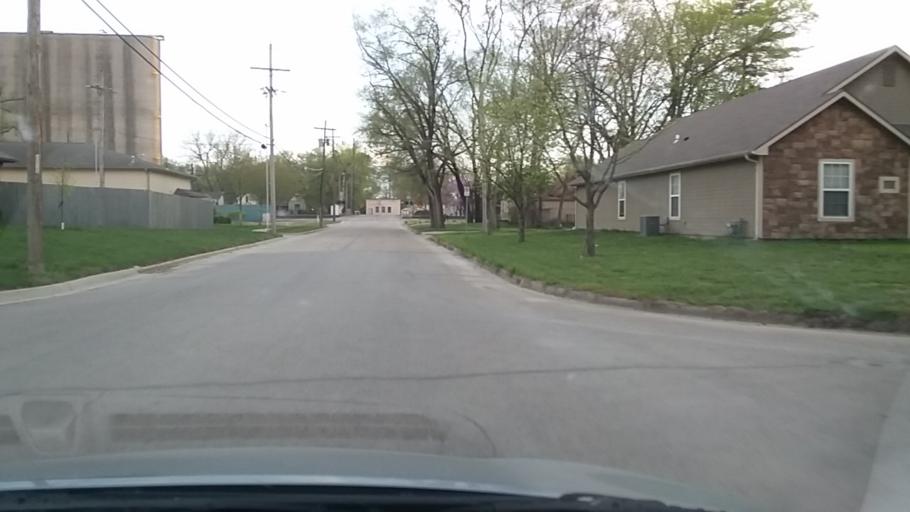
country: US
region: Kansas
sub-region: Douglas County
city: Lawrence
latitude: 38.9797
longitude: -95.2332
